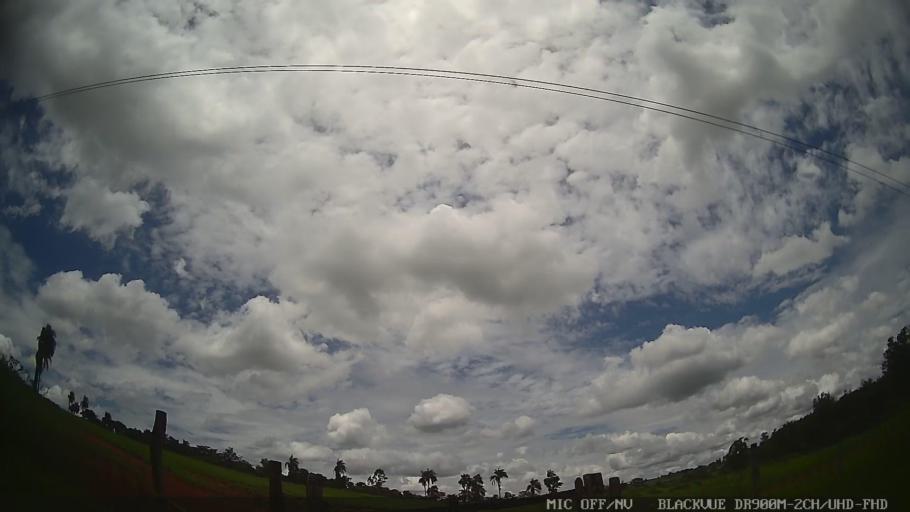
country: BR
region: Sao Paulo
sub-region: Jaguariuna
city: Jaguariuna
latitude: -22.7375
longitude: -47.0057
